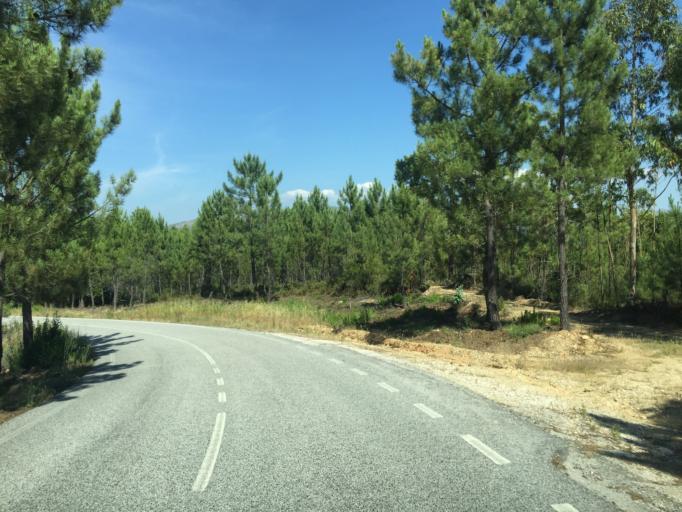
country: PT
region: Castelo Branco
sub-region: Oleiros
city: Oleiros
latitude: 39.9875
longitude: -7.8461
